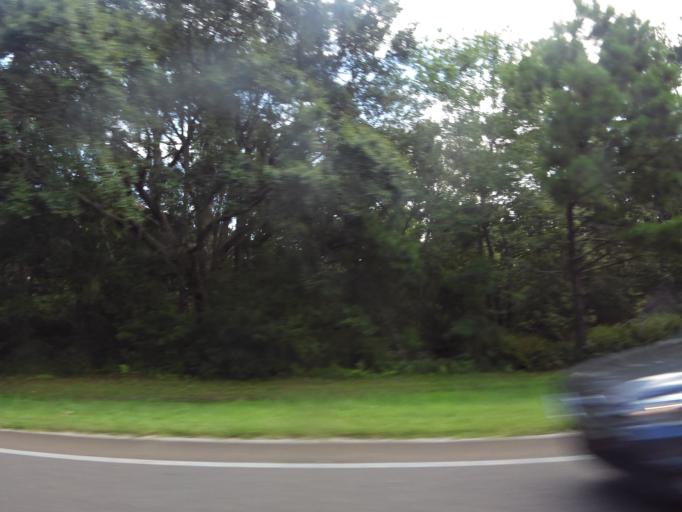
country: US
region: Florida
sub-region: Nassau County
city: Fernandina Beach
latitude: 30.6217
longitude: -81.4638
